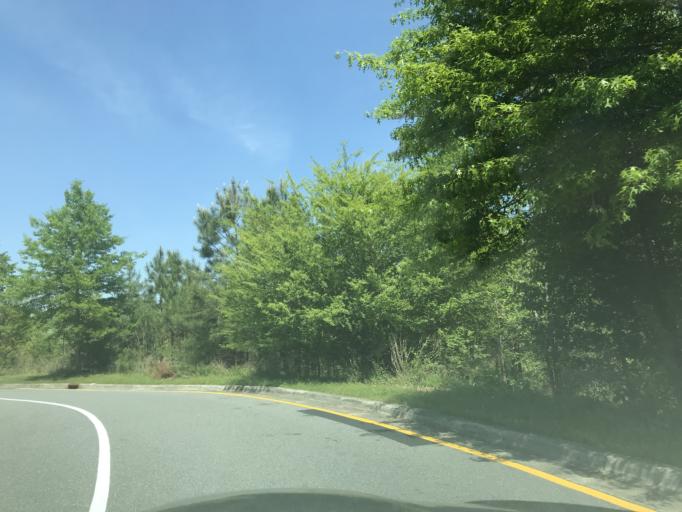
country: US
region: North Carolina
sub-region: Wake County
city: Knightdale
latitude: 35.8645
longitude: -78.5338
